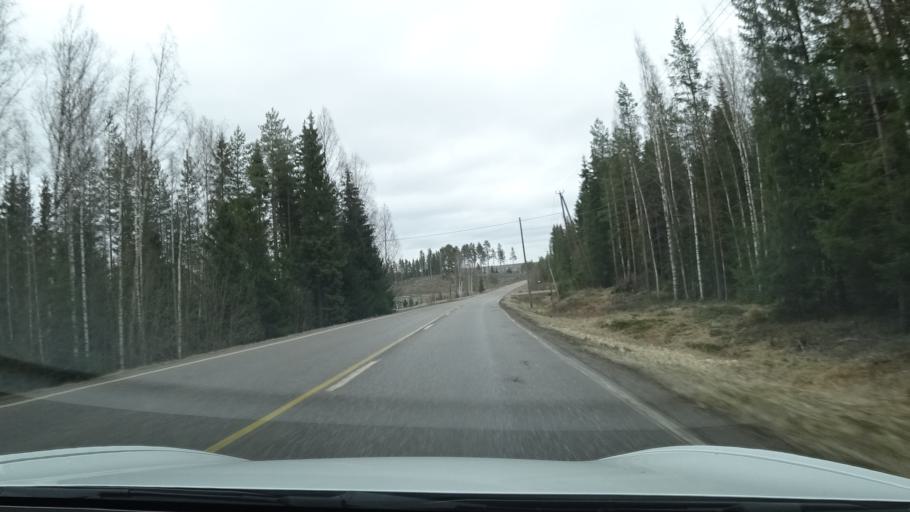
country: FI
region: Uusimaa
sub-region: Porvoo
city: Pukkila
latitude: 60.6500
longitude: 25.6597
